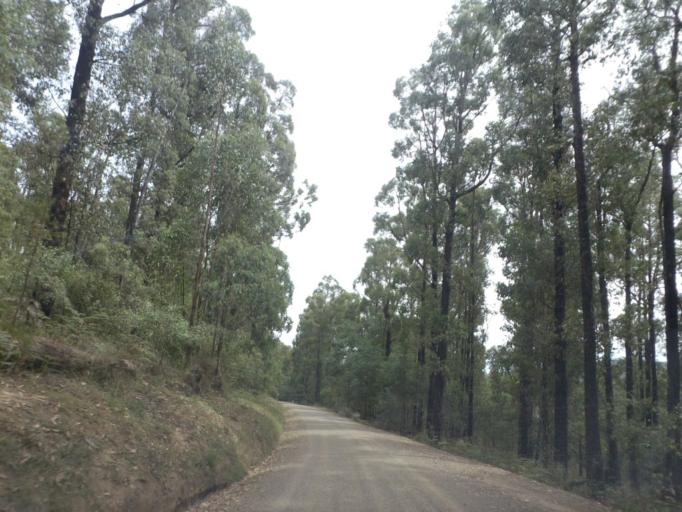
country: AU
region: Victoria
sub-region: Yarra Ranges
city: Healesville
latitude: -37.4360
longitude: 145.5739
